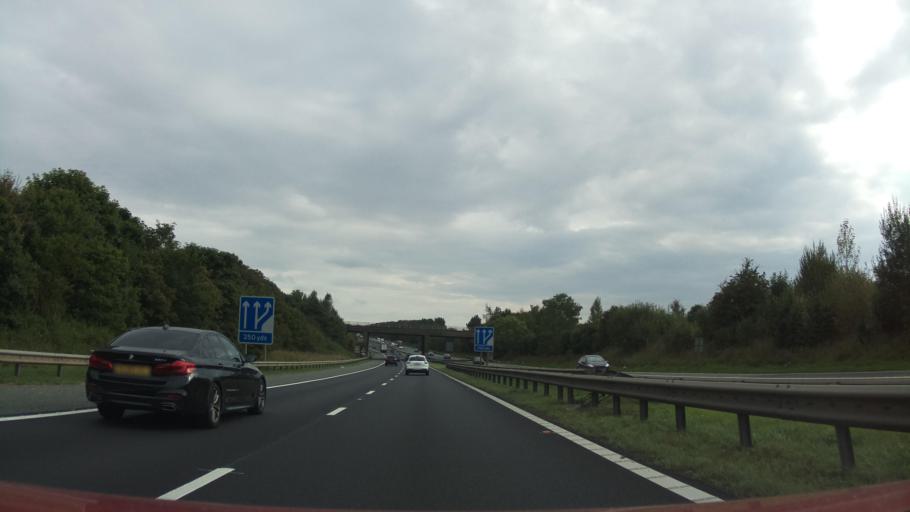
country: GB
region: England
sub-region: County Durham
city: Durham
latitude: 54.7676
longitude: -1.5314
